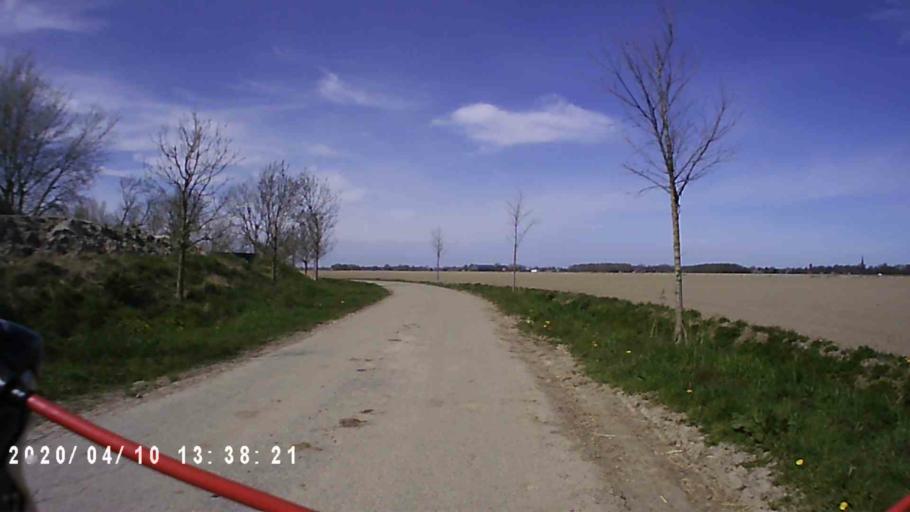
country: NL
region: Groningen
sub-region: Gemeente De Marne
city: Ulrum
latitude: 53.3736
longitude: 6.3975
